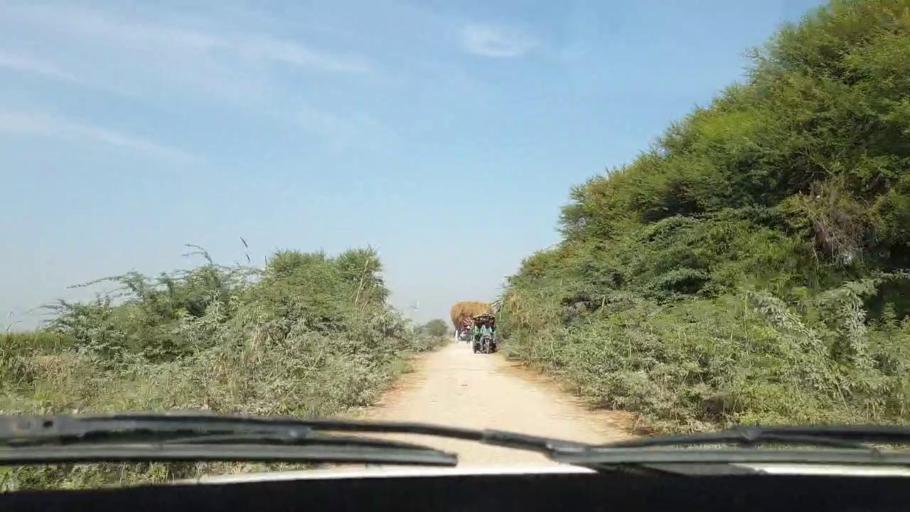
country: PK
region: Sindh
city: Bulri
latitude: 24.8907
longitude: 68.4628
